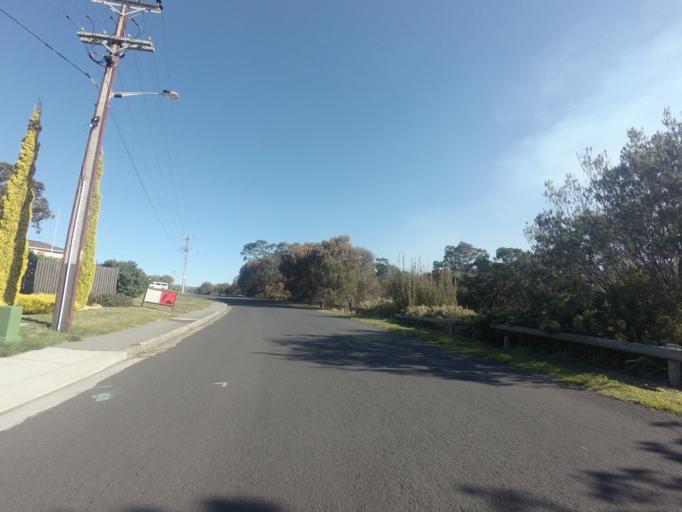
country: AU
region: Tasmania
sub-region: Clarence
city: Bellerive
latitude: -42.8710
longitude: 147.3528
